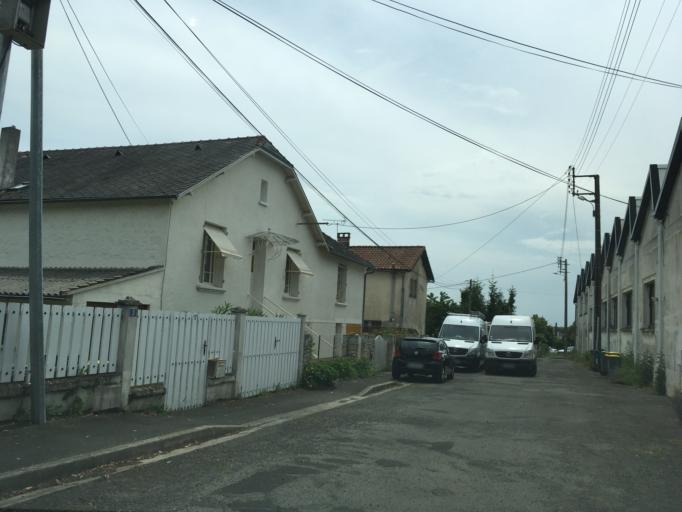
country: FR
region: Poitou-Charentes
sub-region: Departement des Deux-Sevres
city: Niort
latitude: 46.3213
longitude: -0.4754
